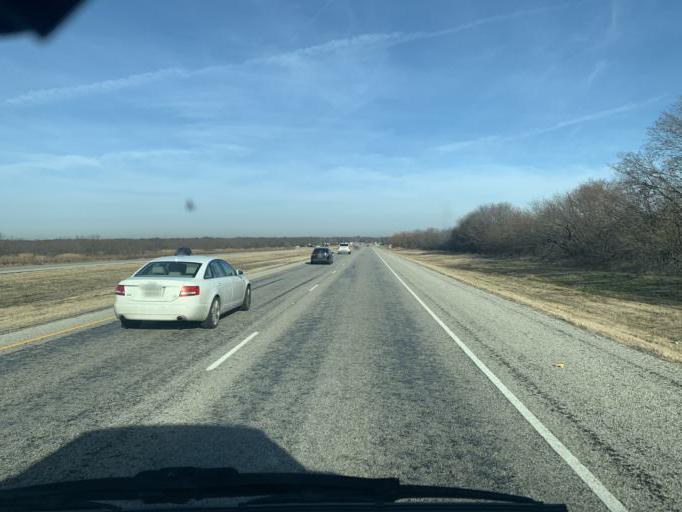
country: US
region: Texas
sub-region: Dallas County
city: Cedar Hill
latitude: 32.6521
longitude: -96.9775
